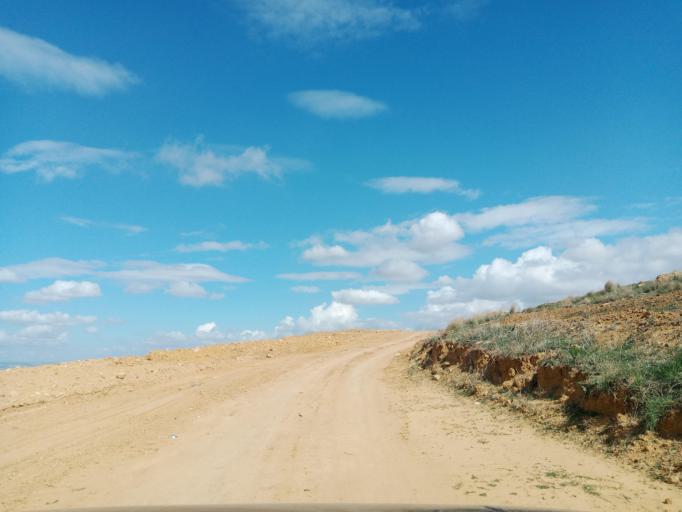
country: TN
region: Tunis
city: Oued Lill
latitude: 36.8154
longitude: 9.9993
